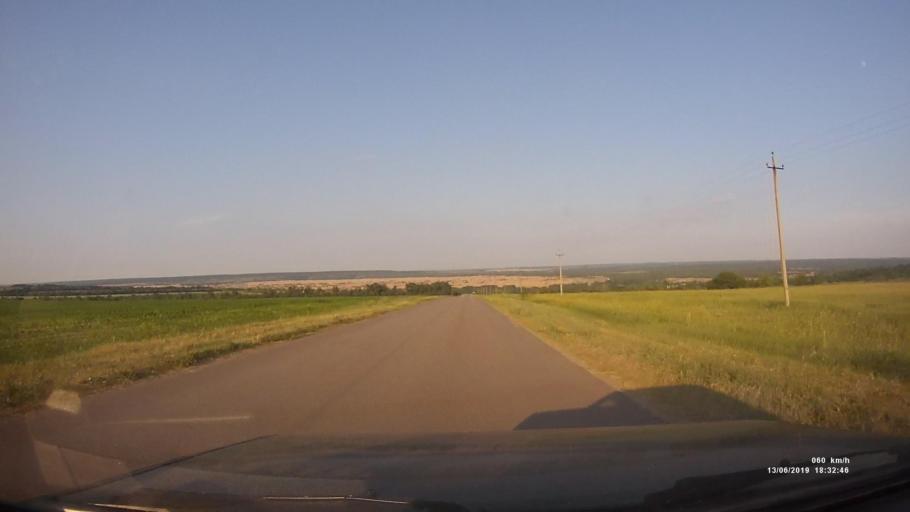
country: RU
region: Rostov
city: Kazanskaya
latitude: 49.8703
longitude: 41.3718
